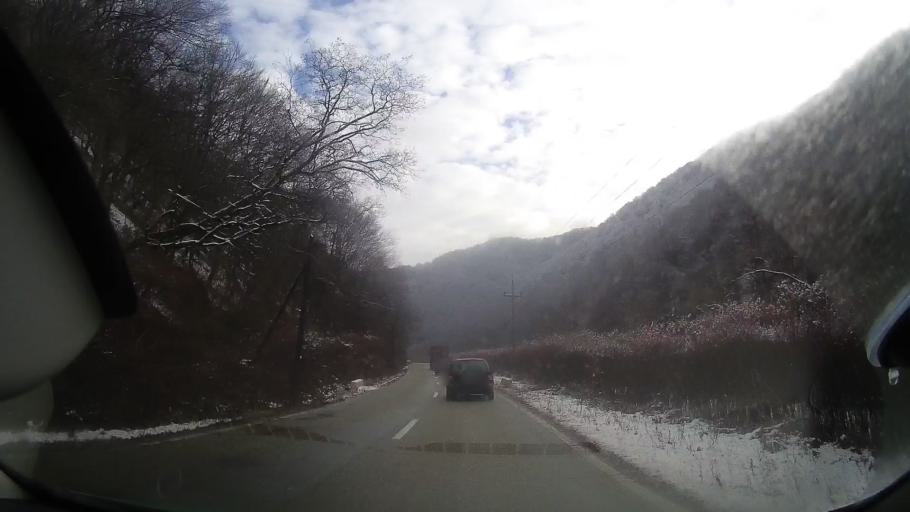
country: RO
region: Alba
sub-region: Oras Baia de Aries
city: Baia de Aries
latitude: 46.4032
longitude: 23.3431
